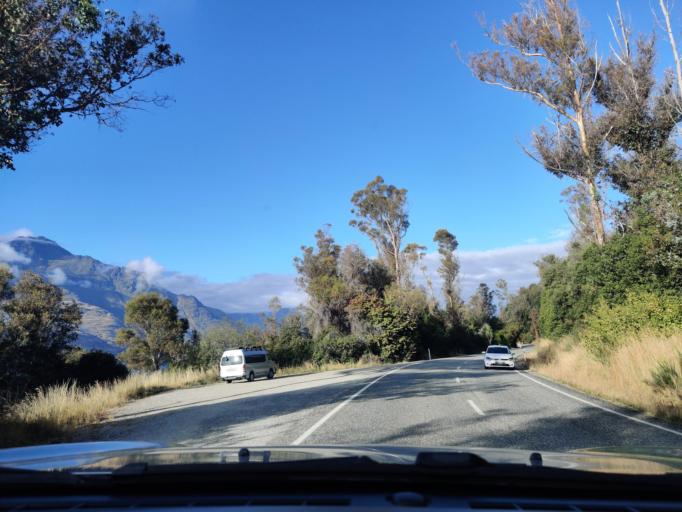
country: NZ
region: Otago
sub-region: Queenstown-Lakes District
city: Queenstown
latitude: -45.0442
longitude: 168.6334
